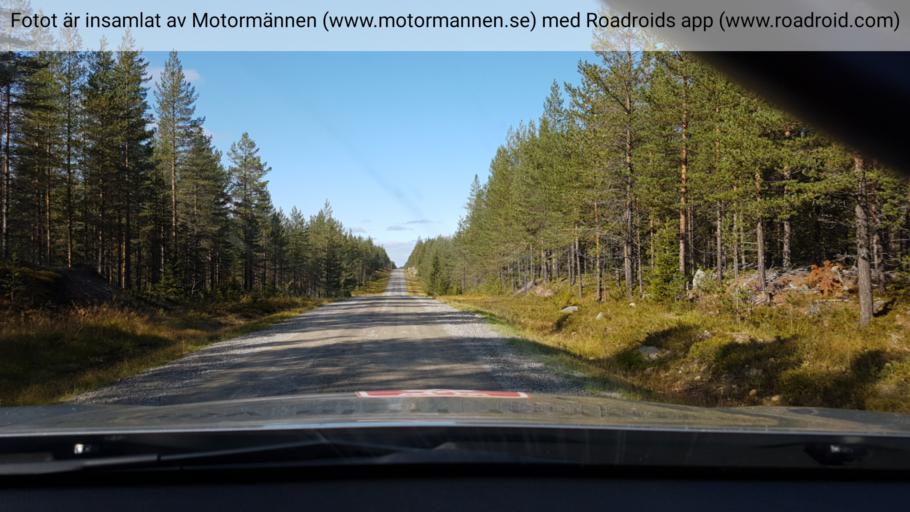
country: SE
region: Norrbotten
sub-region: Arvidsjaurs Kommun
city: Arvidsjaur
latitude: 65.2012
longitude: 19.1807
